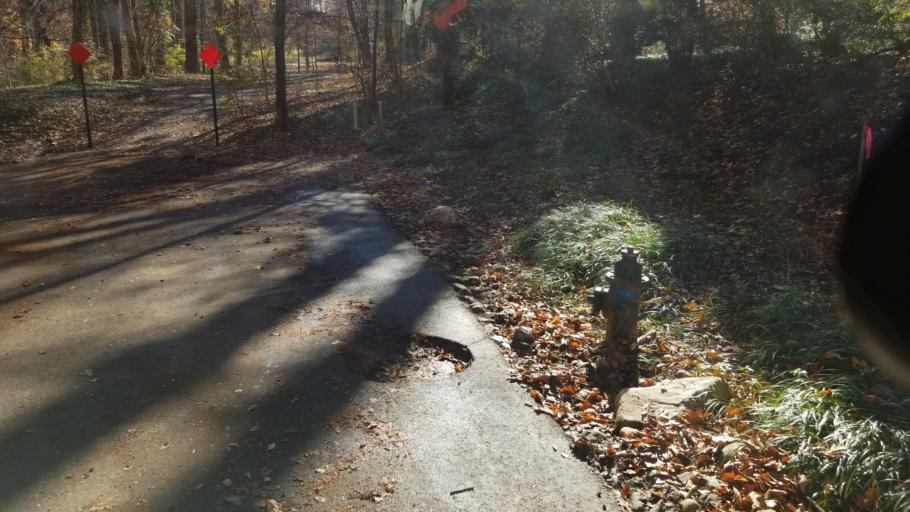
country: US
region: Maryland
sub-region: Montgomery County
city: Brookmont
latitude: 38.9208
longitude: -77.0861
